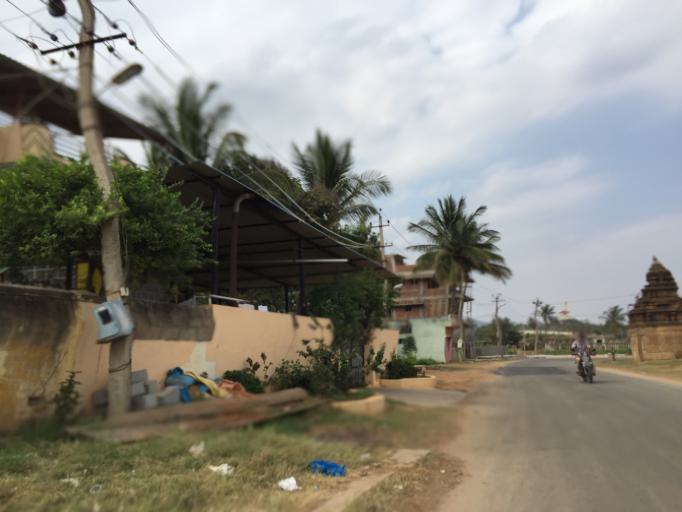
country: IN
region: Karnataka
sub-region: Chikkaballapur
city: Chik Ballapur
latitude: 13.3869
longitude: 77.6977
